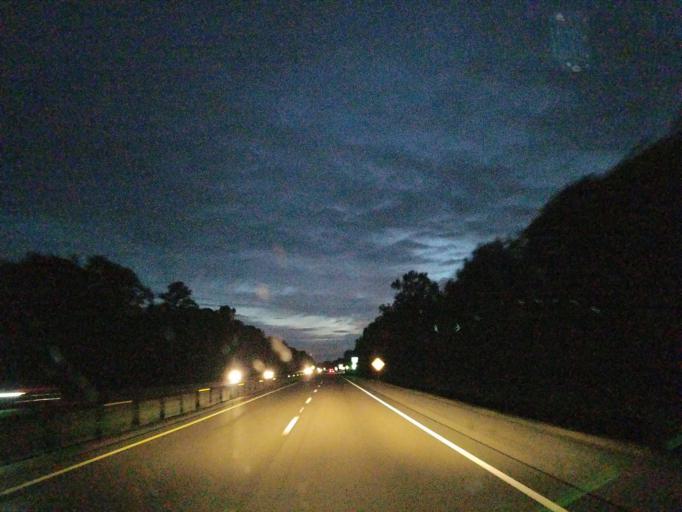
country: US
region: Mississippi
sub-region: Jones County
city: Laurel
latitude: 31.7140
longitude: -89.1095
